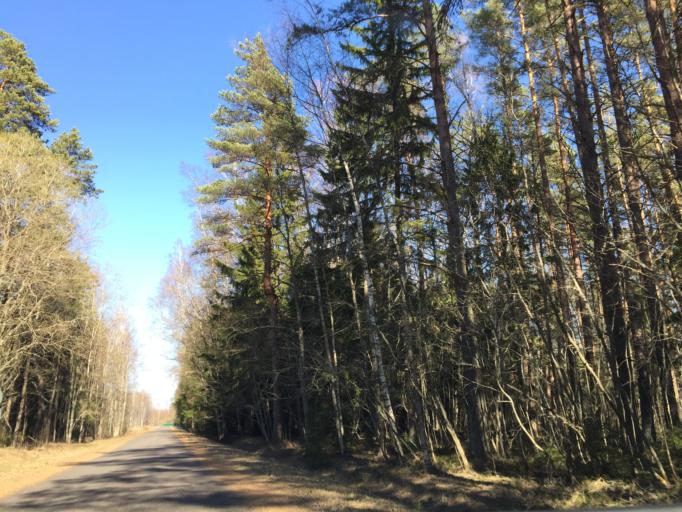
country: EE
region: Ida-Virumaa
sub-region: Johvi vald
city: Johvi
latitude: 59.0097
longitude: 27.5095
